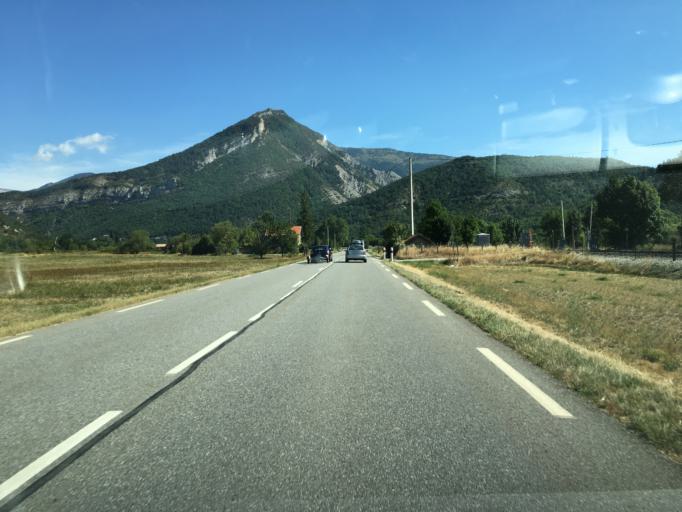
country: FR
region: Provence-Alpes-Cote d'Azur
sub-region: Departement des Hautes-Alpes
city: Veynes
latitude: 44.5330
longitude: 5.7729
